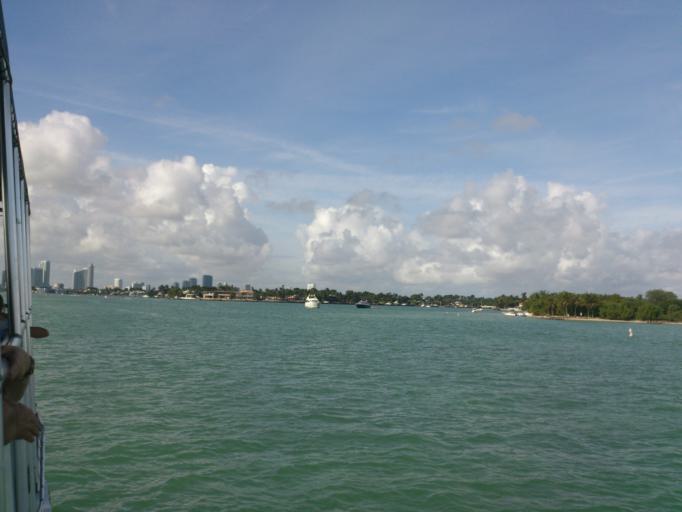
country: US
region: Florida
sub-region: Miami-Dade County
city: Miami Beach
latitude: 25.7823
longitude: -80.1518
